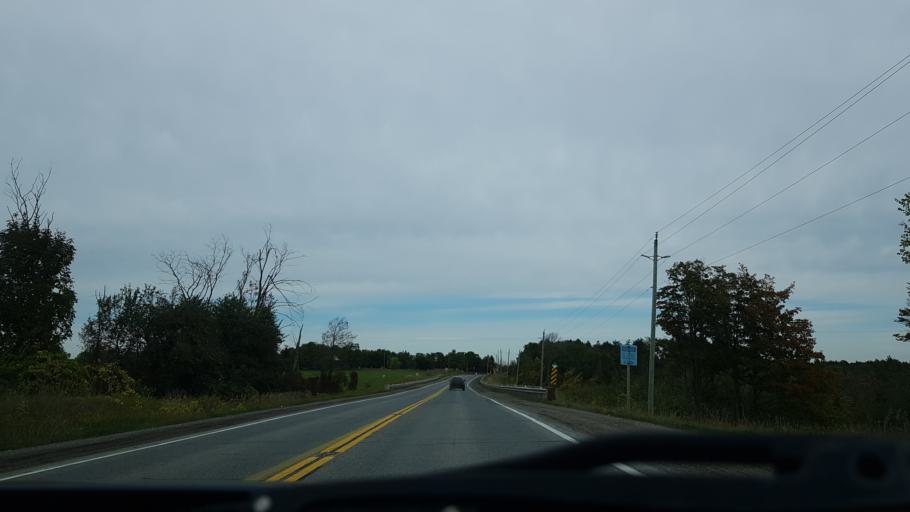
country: CA
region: Ontario
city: Orangeville
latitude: 43.9134
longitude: -79.9353
